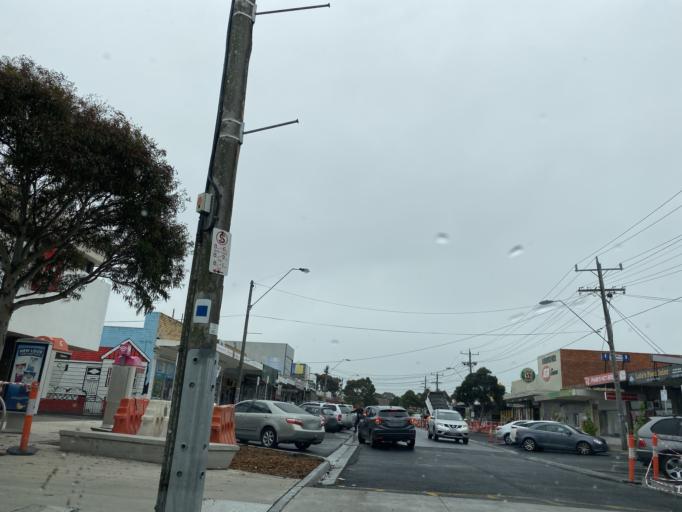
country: AU
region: Victoria
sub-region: Moreland
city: Fawkner
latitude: -37.7030
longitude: 144.9654
